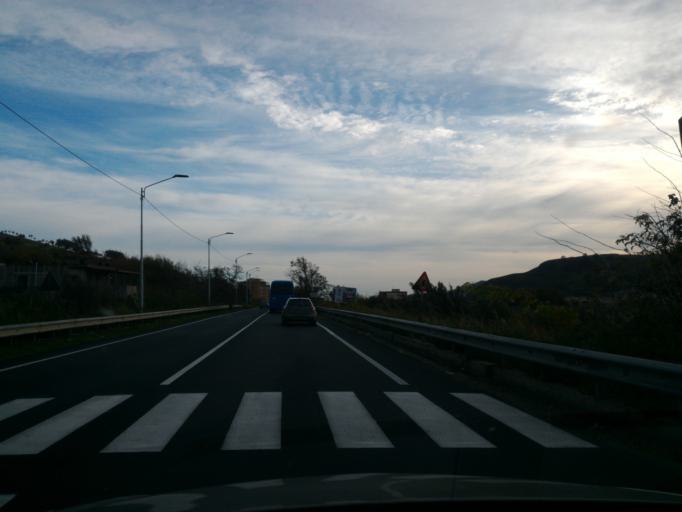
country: IT
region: Calabria
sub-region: Provincia di Catanzaro
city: Catanzaro
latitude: 38.8751
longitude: 16.6044
